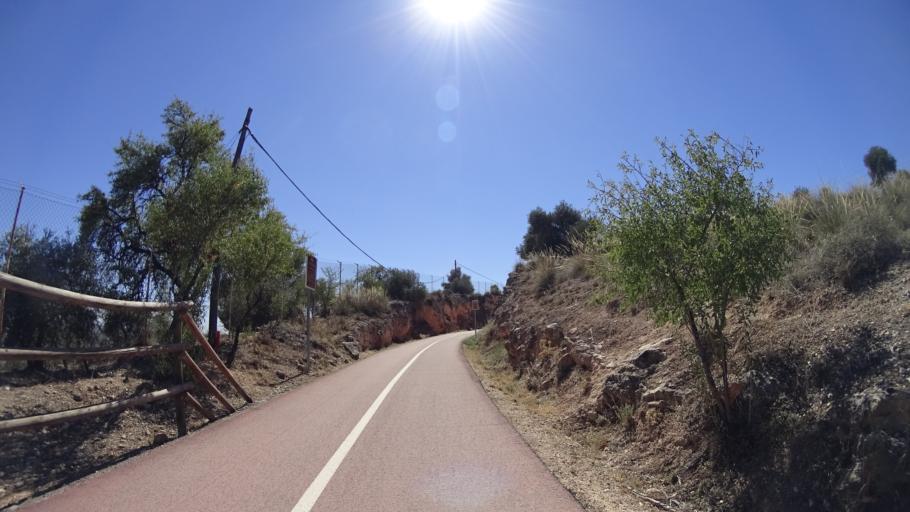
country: ES
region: Madrid
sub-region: Provincia de Madrid
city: Morata de Tajuna
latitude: 40.2312
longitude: -3.4480
